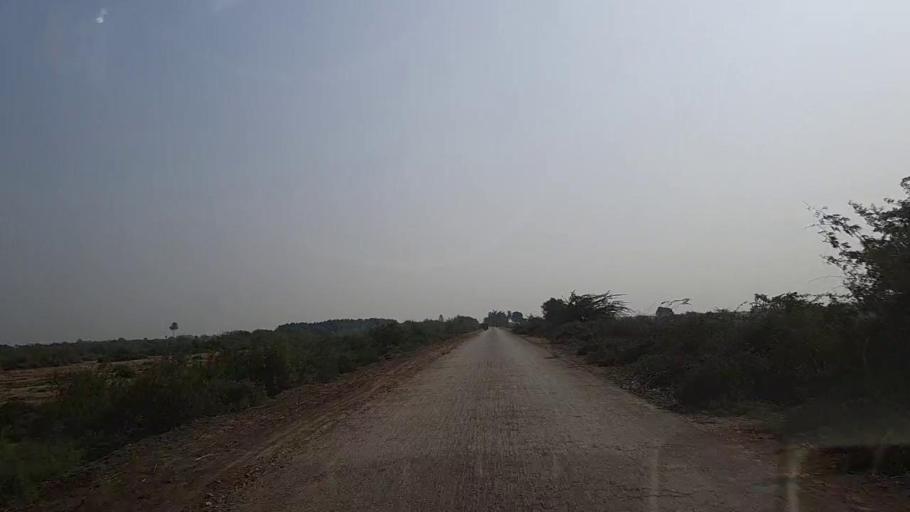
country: PK
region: Sindh
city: Keti Bandar
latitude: 24.2411
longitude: 67.6377
